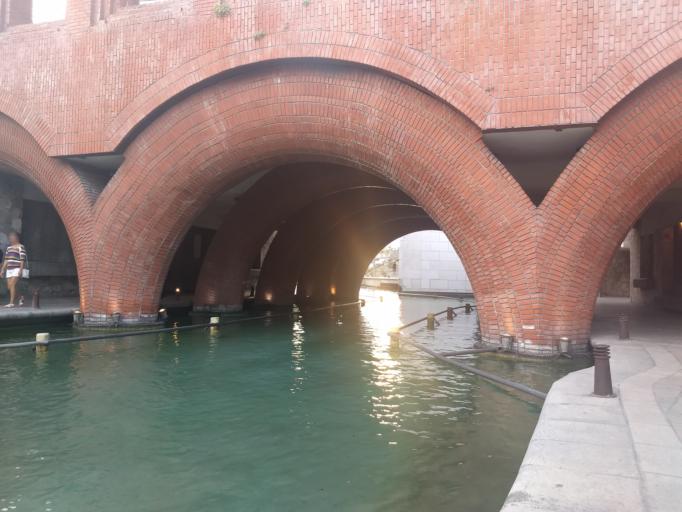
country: MX
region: Nuevo Leon
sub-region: Monterrey
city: Monterrey
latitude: 25.6710
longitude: -100.3059
